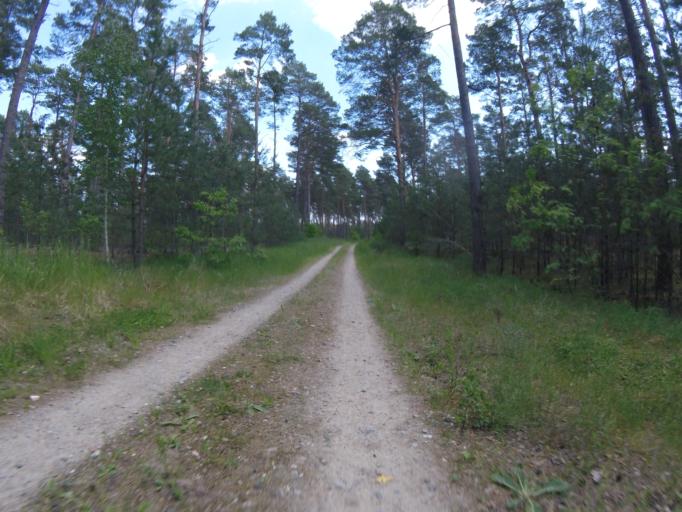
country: DE
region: Brandenburg
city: Teupitz
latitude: 52.1026
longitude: 13.6032
